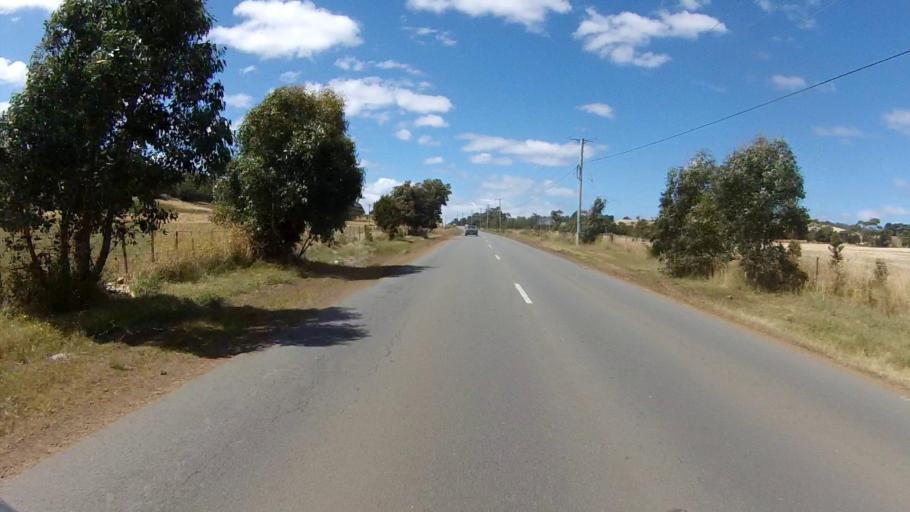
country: AU
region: Tasmania
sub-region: Clarence
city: Cambridge
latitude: -42.8183
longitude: 147.4382
